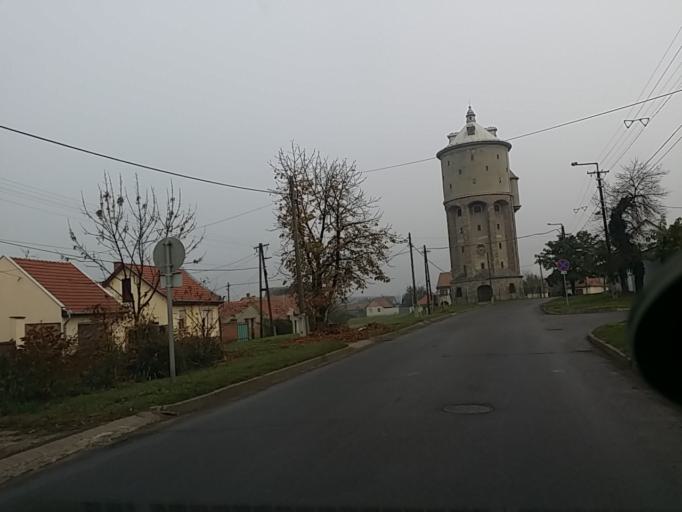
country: HU
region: Heves
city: Gyongyos
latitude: 47.7931
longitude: 19.9286
